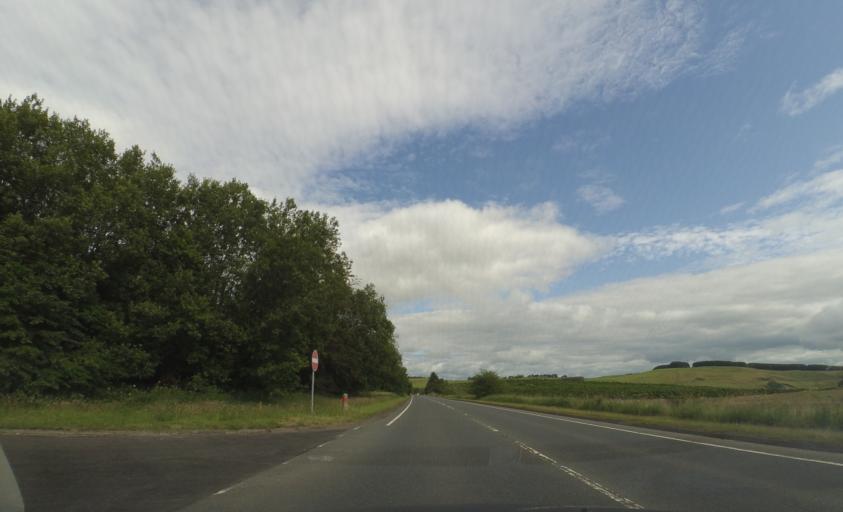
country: GB
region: Scotland
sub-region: The Scottish Borders
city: Selkirk
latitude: 55.5264
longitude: -2.8261
